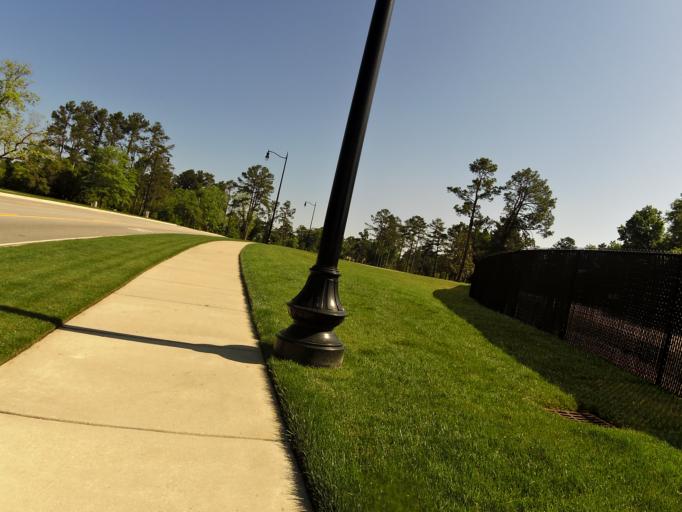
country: US
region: Georgia
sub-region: Columbia County
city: Martinez
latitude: 33.4989
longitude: -82.0312
